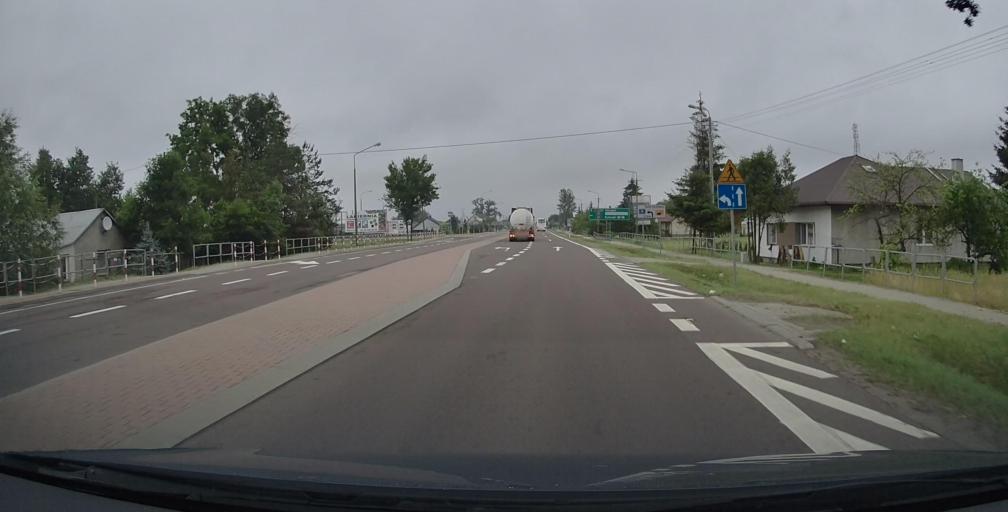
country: PL
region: Lublin Voivodeship
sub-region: Powiat bialski
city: Zalesie
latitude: 52.0371
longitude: 23.4689
